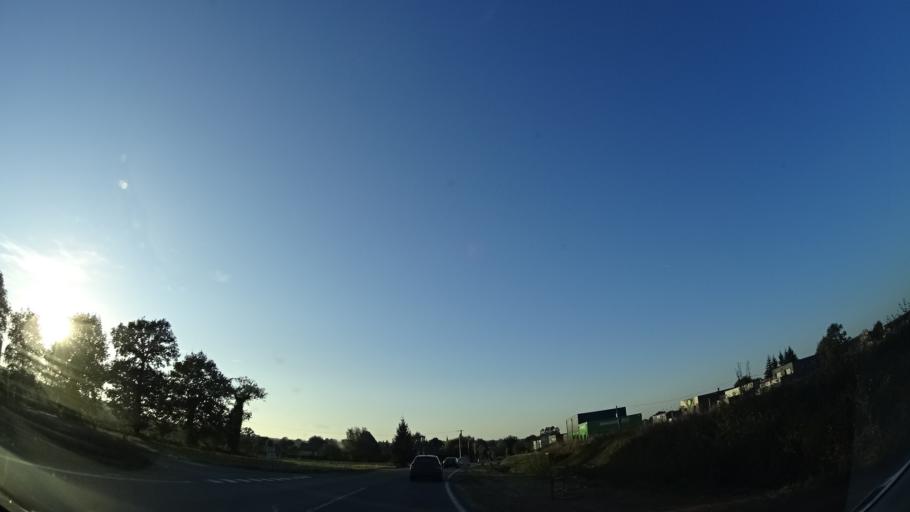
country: FR
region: Brittany
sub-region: Departement d'Ille-et-Vilaine
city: Geveze
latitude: 48.2145
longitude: -1.7751
